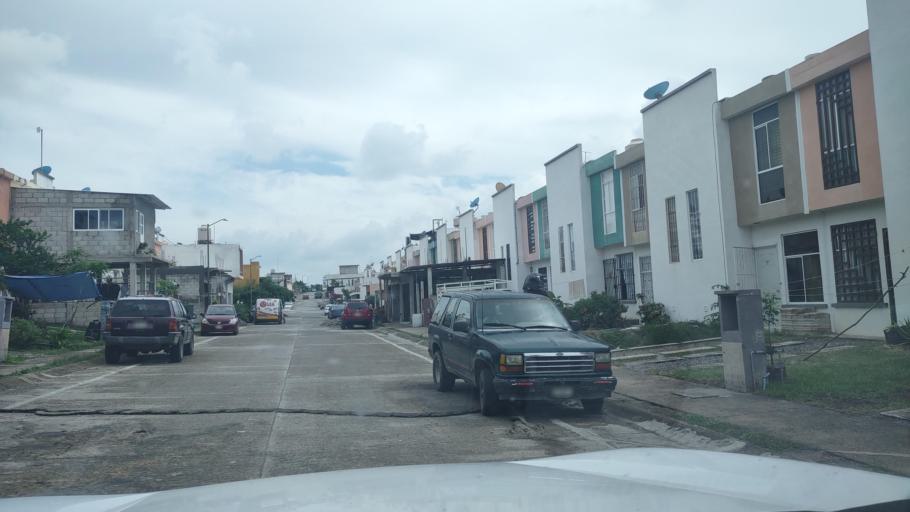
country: MX
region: Veracruz
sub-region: Tuxpan
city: Alto Lucero
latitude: 20.9587
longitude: -97.4381
